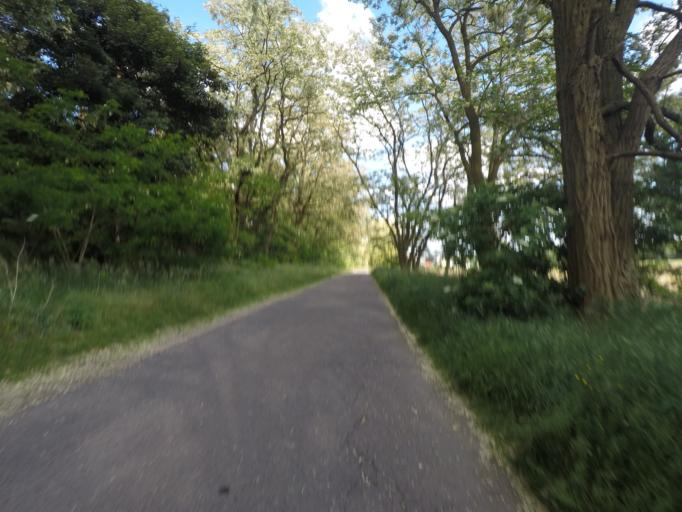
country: DE
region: Brandenburg
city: Britz
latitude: 52.8697
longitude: 13.7644
